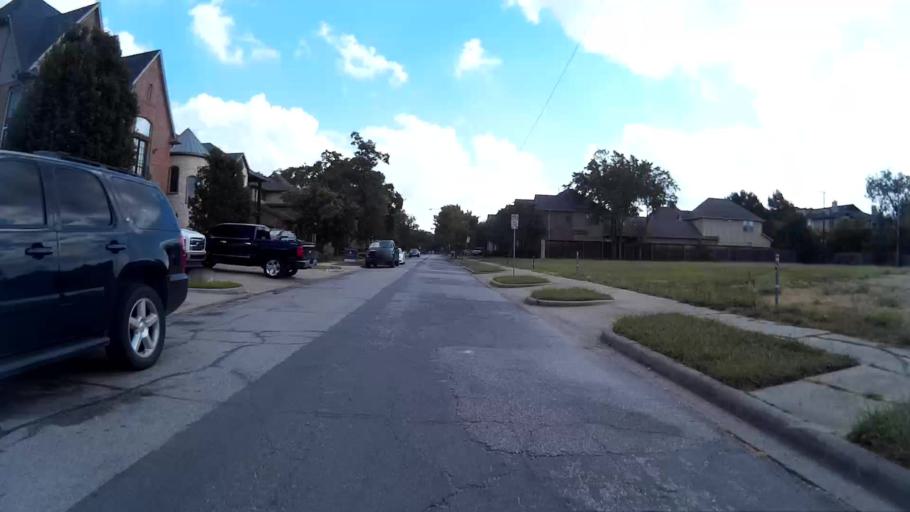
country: US
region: Texas
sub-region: Dallas County
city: Highland Park
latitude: 32.8213
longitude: -96.7843
